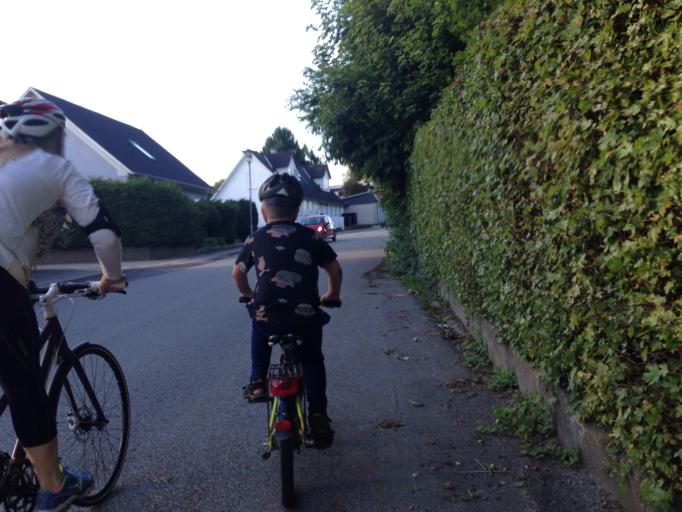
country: DK
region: South Denmark
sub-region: Middelfart Kommune
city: Norre Aby
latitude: 55.4863
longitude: 9.9074
